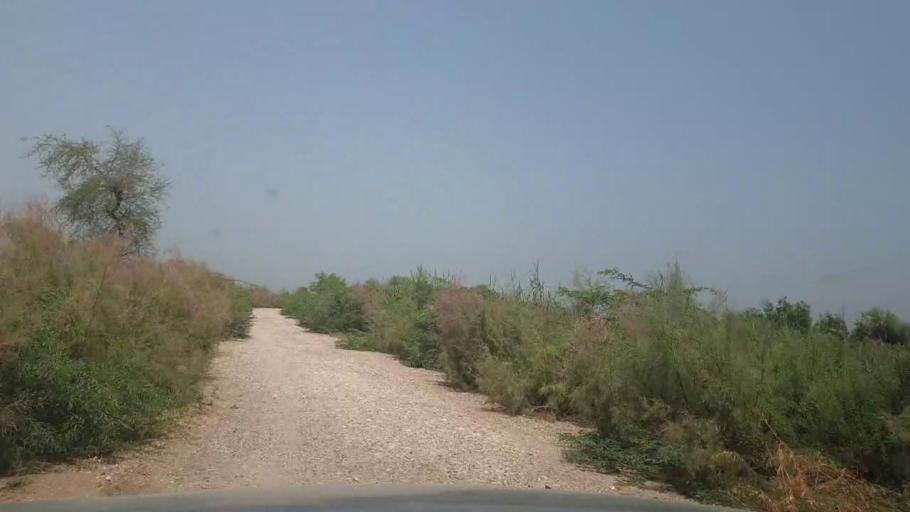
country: PK
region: Sindh
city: Lakhi
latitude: 27.8309
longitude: 68.6232
